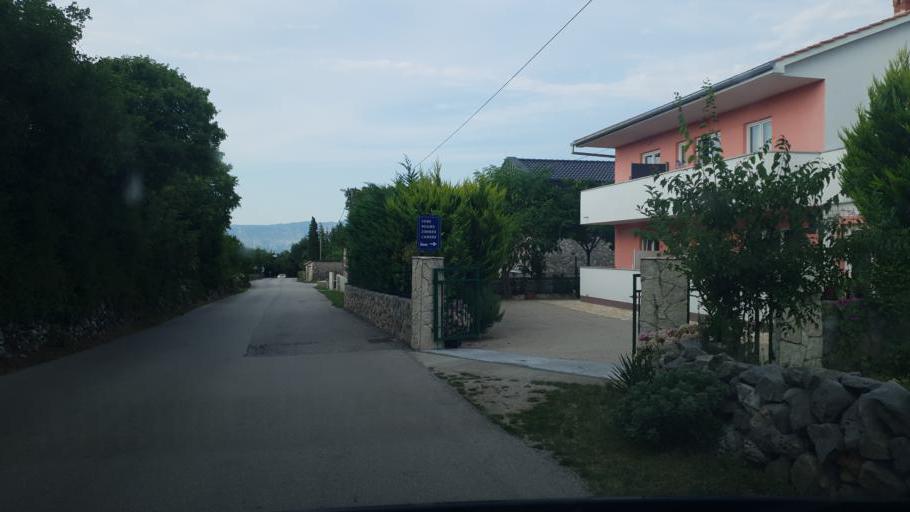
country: HR
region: Primorsko-Goranska
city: Njivice
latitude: 45.1245
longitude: 14.5681
